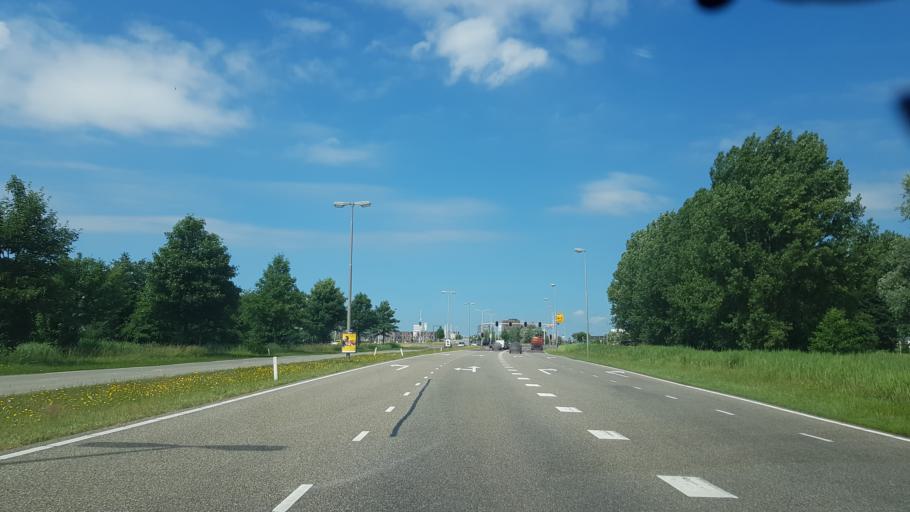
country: NL
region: Friesland
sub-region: Gemeente Leeuwarden
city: Camminghaburen
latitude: 53.2151
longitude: 5.8292
